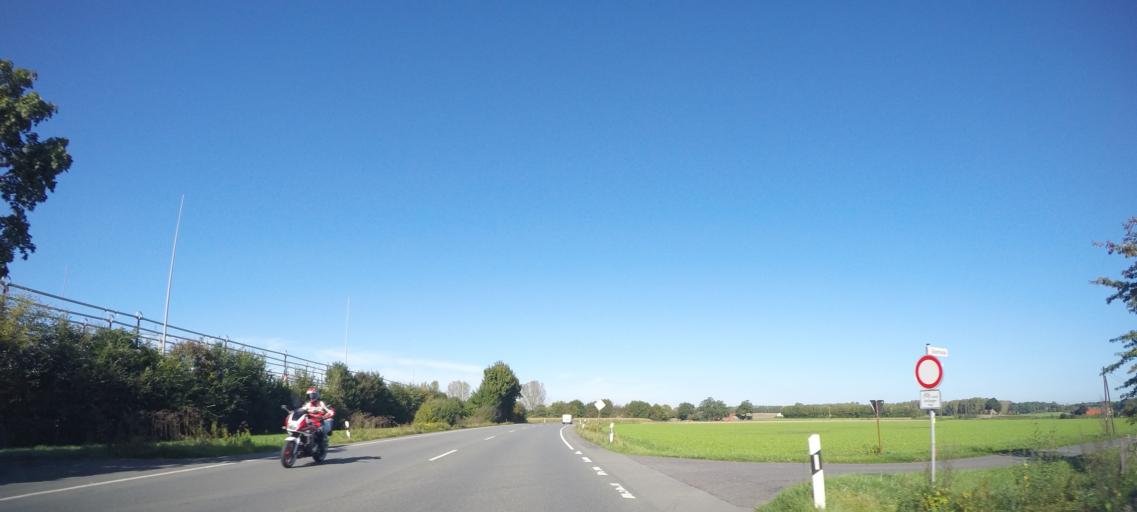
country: DE
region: North Rhine-Westphalia
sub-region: Regierungsbezirk Arnsberg
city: Welver
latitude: 51.6839
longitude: 7.9948
